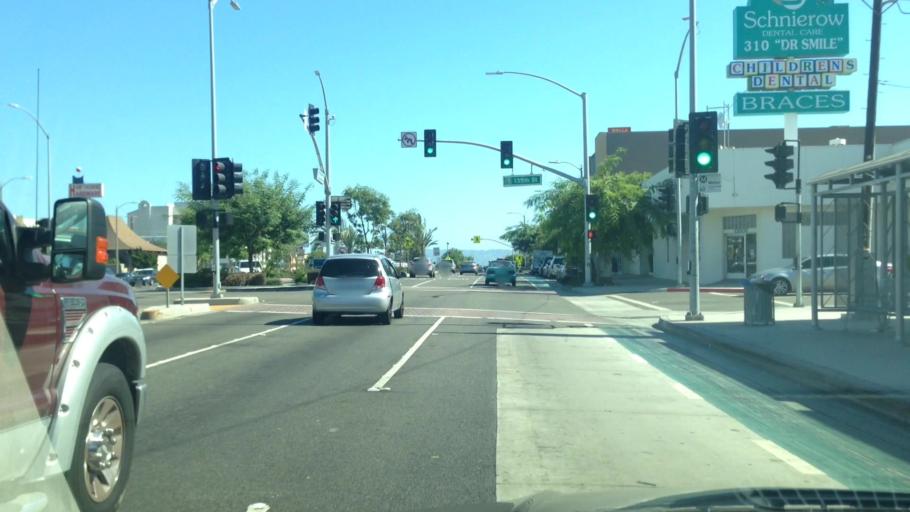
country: US
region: California
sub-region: Los Angeles County
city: Hawthorne
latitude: 33.9102
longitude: -118.3528
